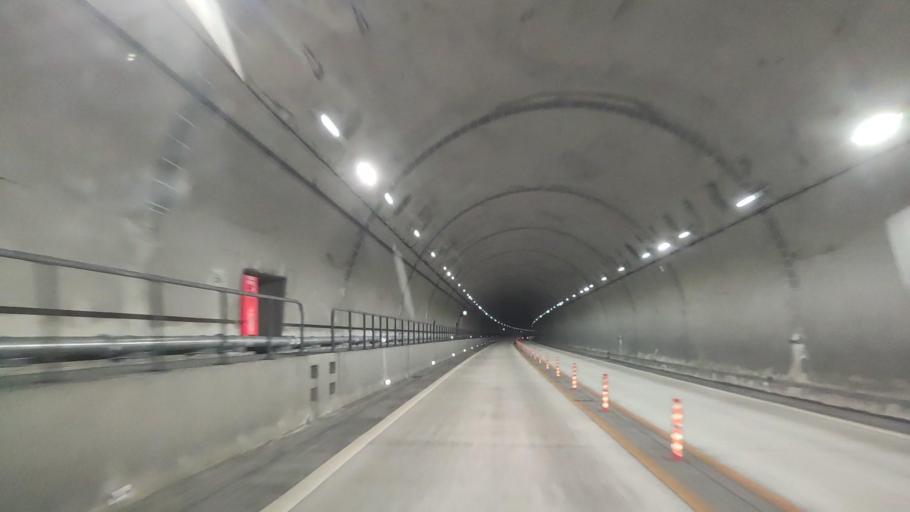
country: JP
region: Ehime
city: Hojo
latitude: 34.0783
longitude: 132.9761
